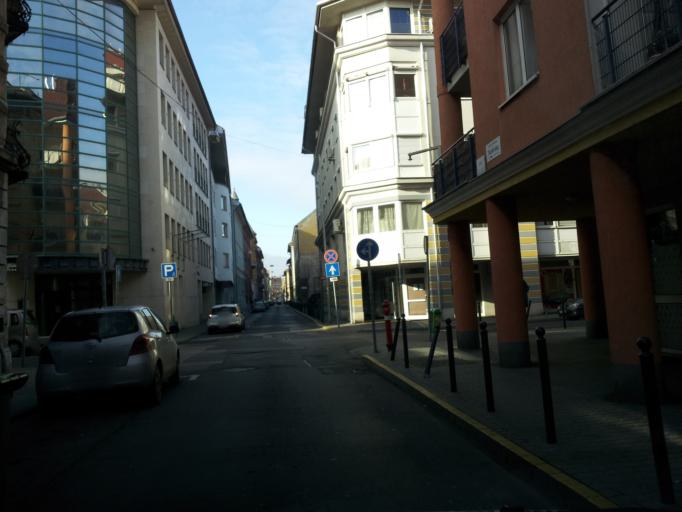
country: HU
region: Budapest
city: Budapest VIII. keruelet
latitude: 47.4821
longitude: 19.0767
